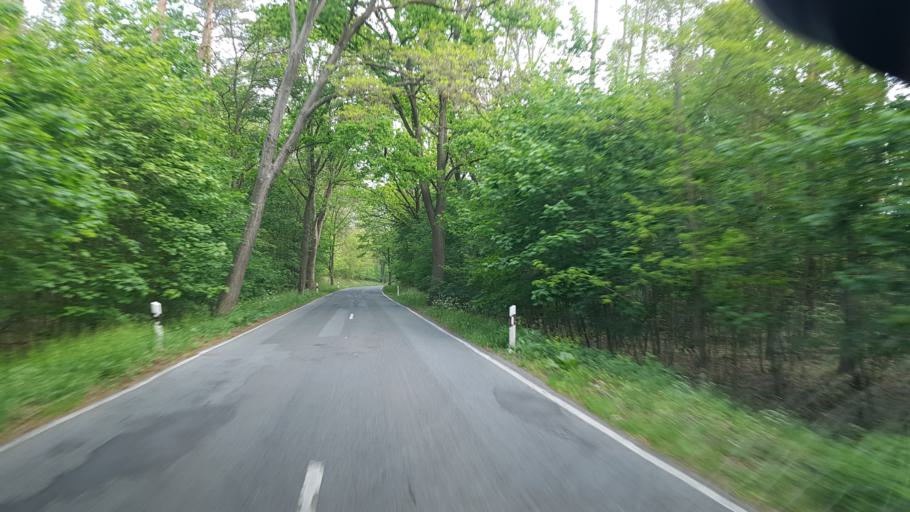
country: DE
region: Brandenburg
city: Baruth
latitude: 52.0197
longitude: 13.4696
